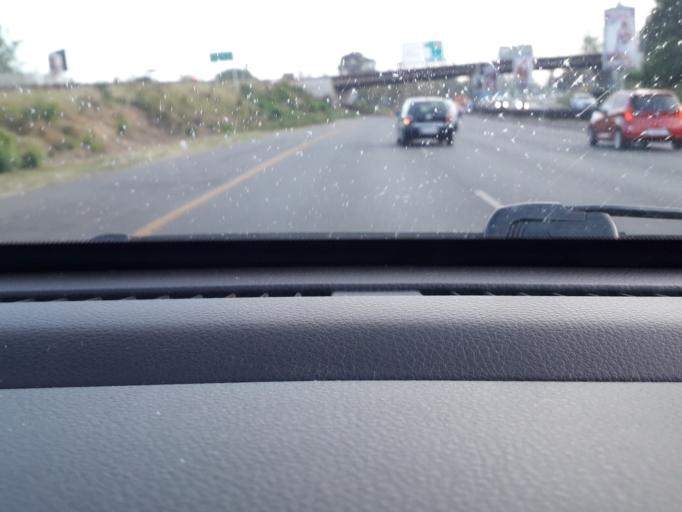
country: ZA
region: Gauteng
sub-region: City of Johannesburg Metropolitan Municipality
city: Johannesburg
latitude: -26.1476
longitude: 28.0575
